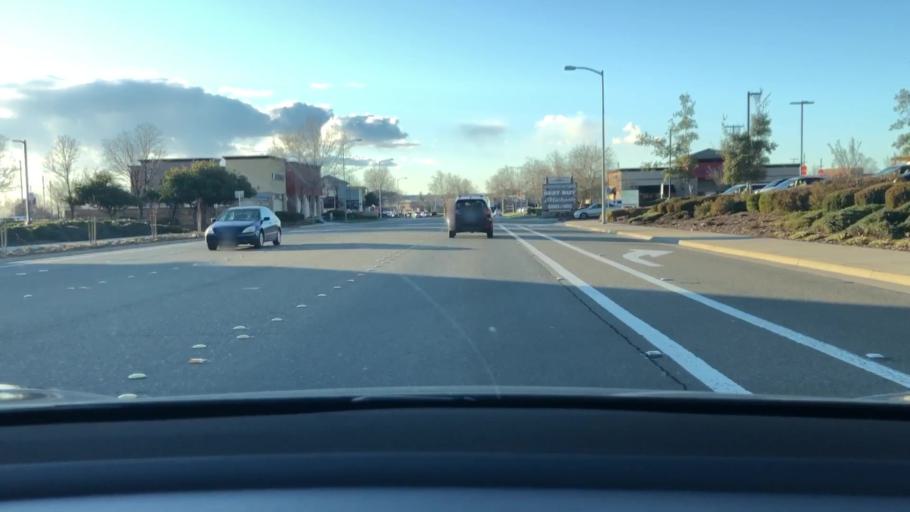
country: US
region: California
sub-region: Placer County
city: Roseville
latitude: 38.7711
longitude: -121.2622
